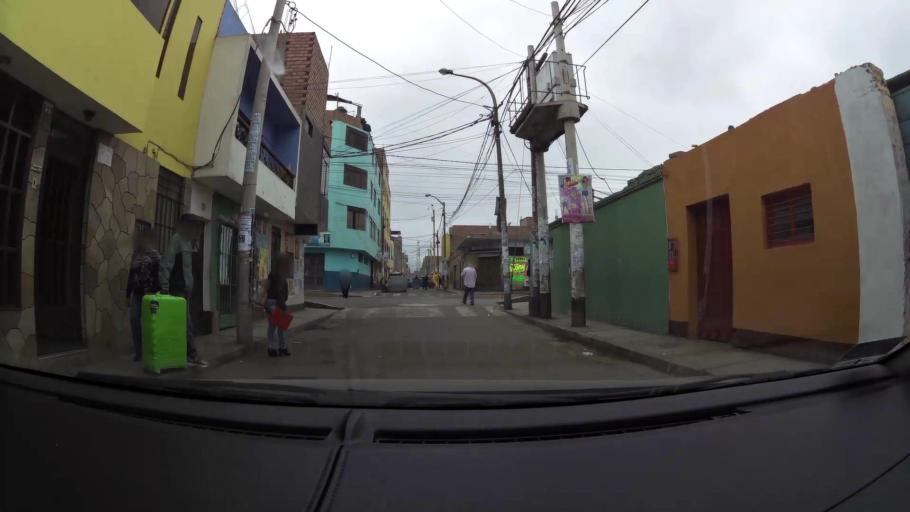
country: PE
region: Lima
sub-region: Provincia de Huaral
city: Huaral
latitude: -11.4975
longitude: -77.2093
